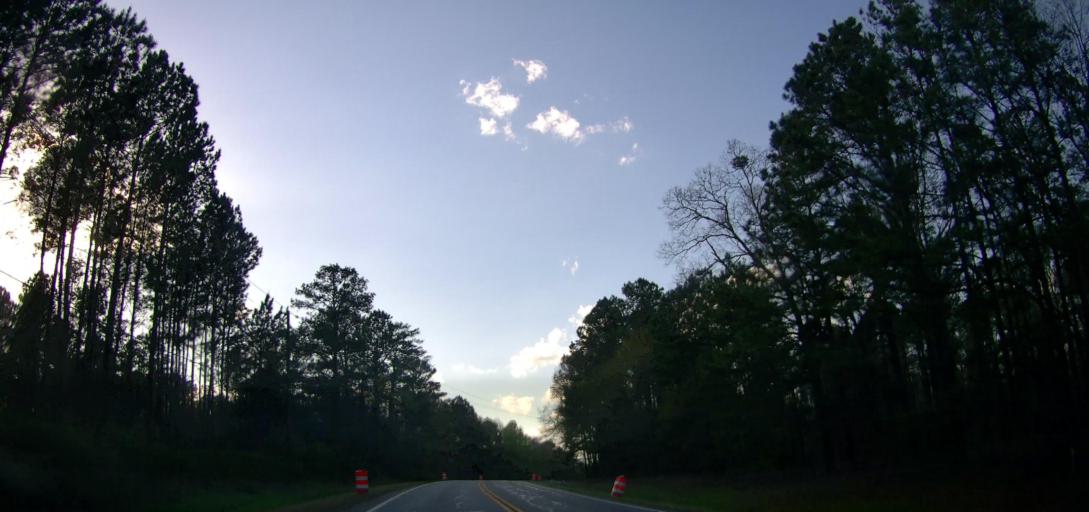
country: US
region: Georgia
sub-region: Putnam County
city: Eatonton
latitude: 33.1764
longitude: -83.4036
